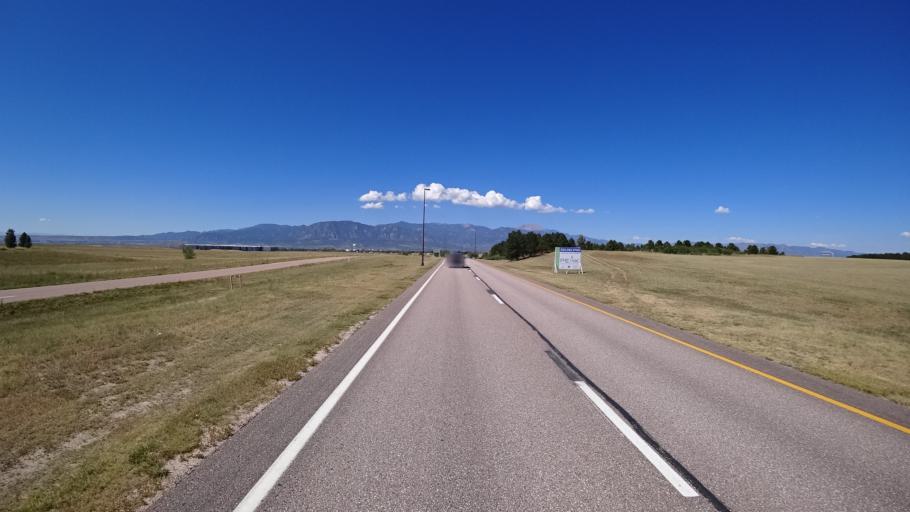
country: US
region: Colorado
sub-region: El Paso County
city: Security-Widefield
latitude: 38.7812
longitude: -104.7015
